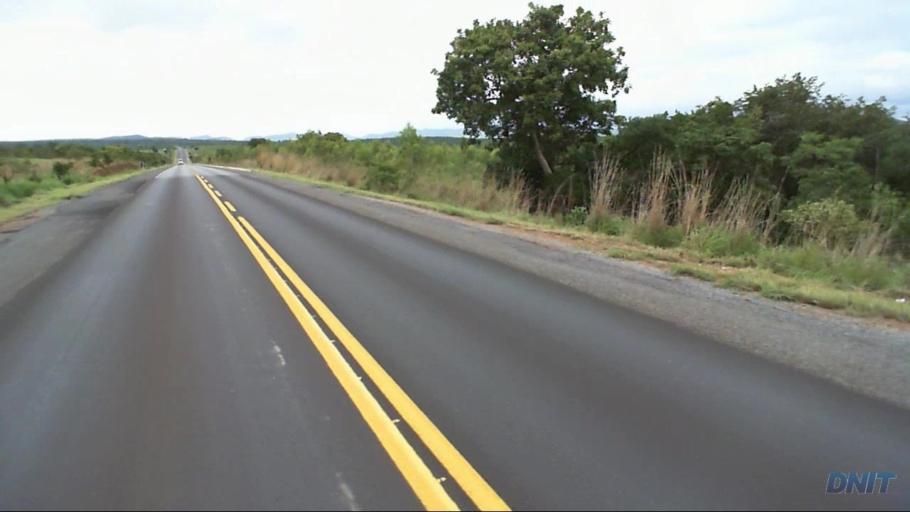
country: BR
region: Goias
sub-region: Barro Alto
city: Barro Alto
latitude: -15.2179
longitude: -48.6514
